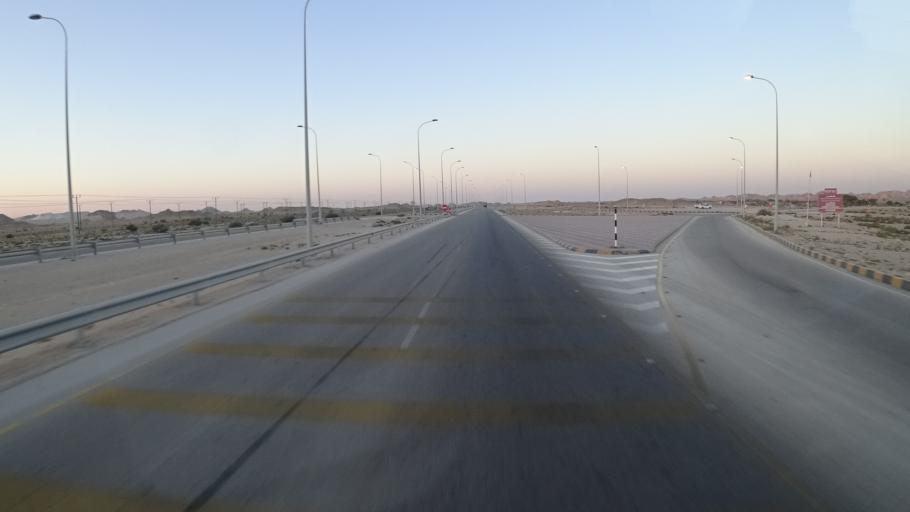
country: OM
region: Zufar
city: Salalah
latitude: 17.4692
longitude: 54.0497
